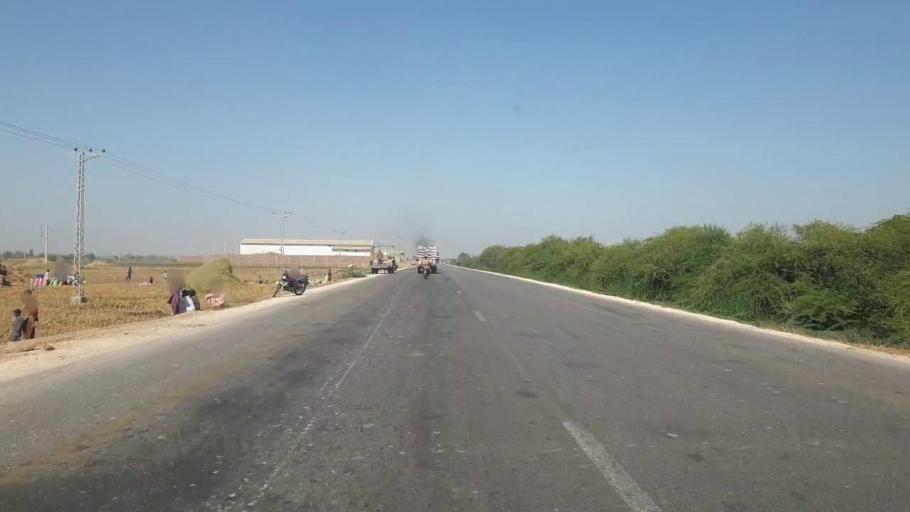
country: PK
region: Sindh
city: Talhar
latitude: 24.8631
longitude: 68.8166
